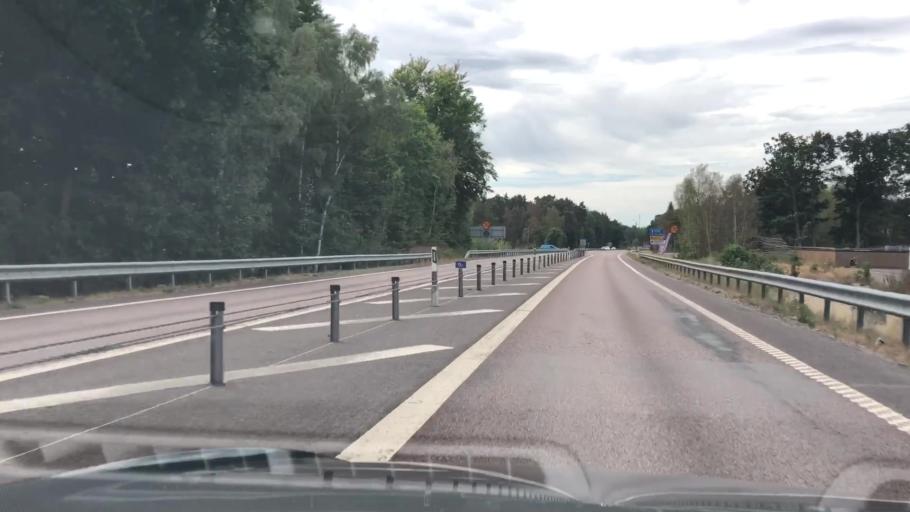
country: SE
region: Kalmar
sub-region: Torsas Kommun
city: Torsas
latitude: 56.3037
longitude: 16.0079
